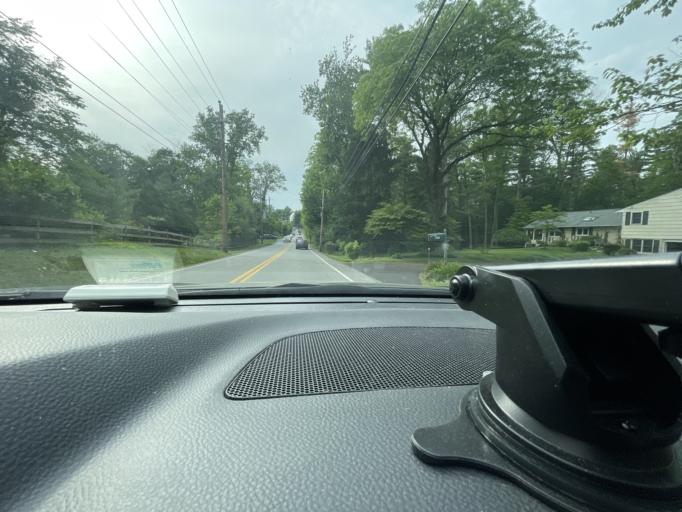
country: US
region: Pennsylvania
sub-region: Montgomery County
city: Blue Bell
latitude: 40.1650
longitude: -75.2613
